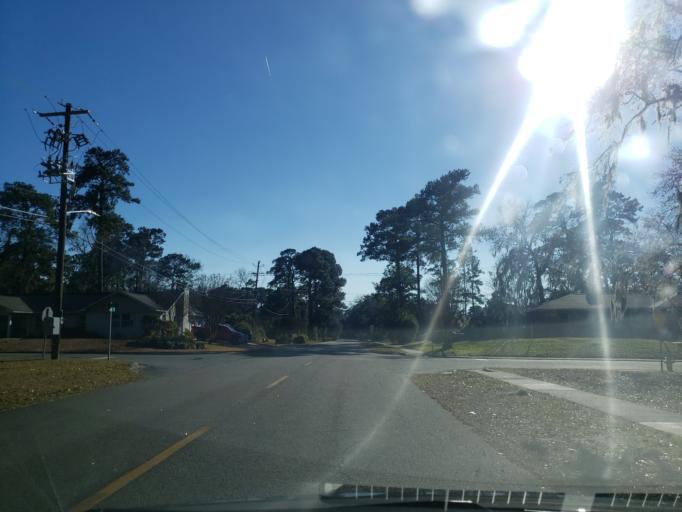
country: US
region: Georgia
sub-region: Chatham County
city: Thunderbolt
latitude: 32.0201
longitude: -81.1022
